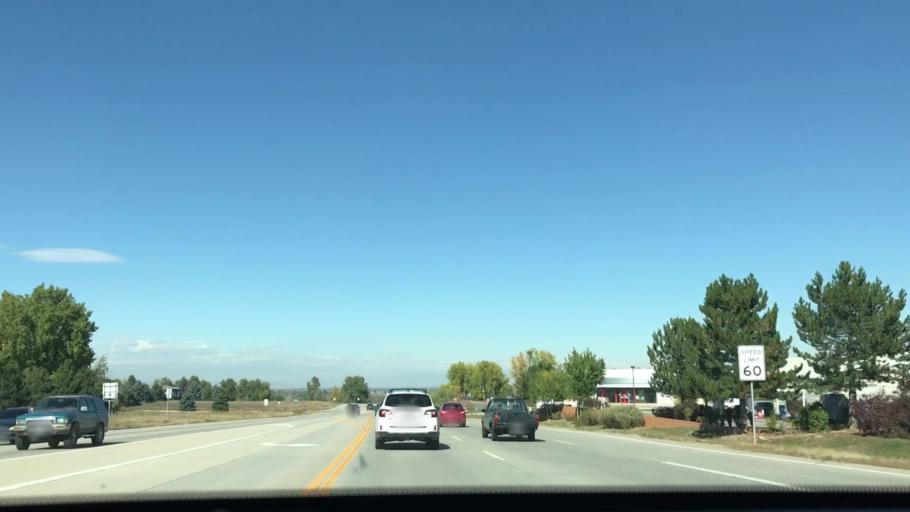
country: US
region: Colorado
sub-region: Boulder County
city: Lafayette
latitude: 40.0159
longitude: -105.1022
